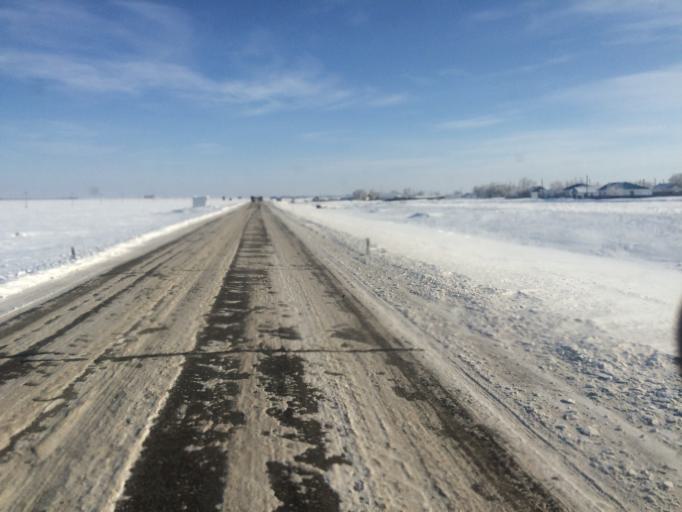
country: RU
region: Orenburg
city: Dombarovskiy
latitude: 49.9738
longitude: 60.0395
